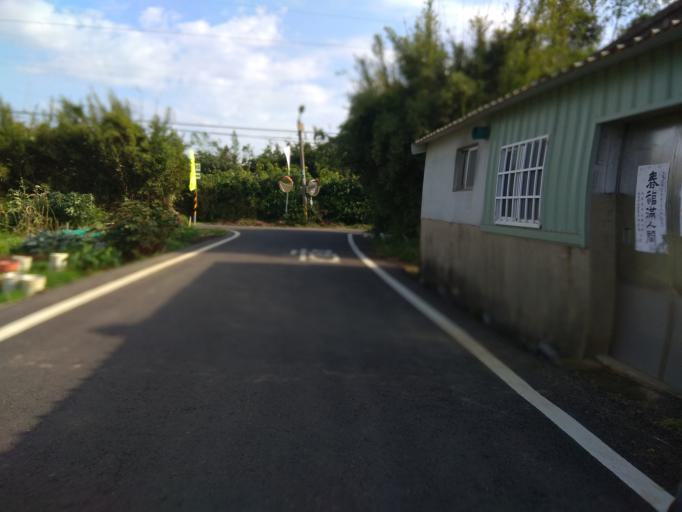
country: TW
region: Taiwan
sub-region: Hsinchu
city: Zhubei
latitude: 25.0002
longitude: 121.0450
